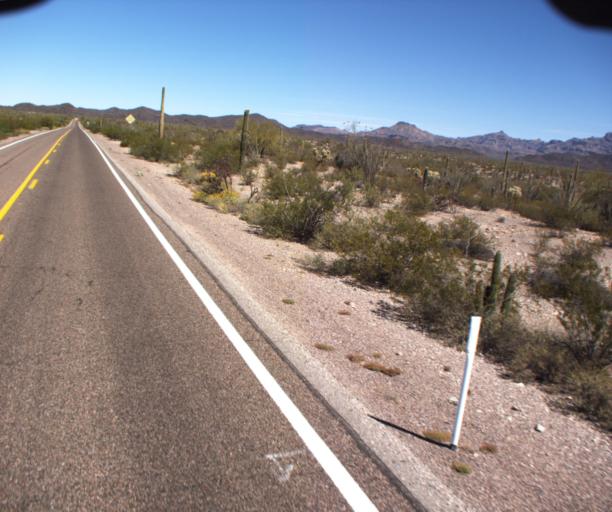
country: MX
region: Sonora
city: Sonoyta
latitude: 31.9405
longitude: -112.7987
